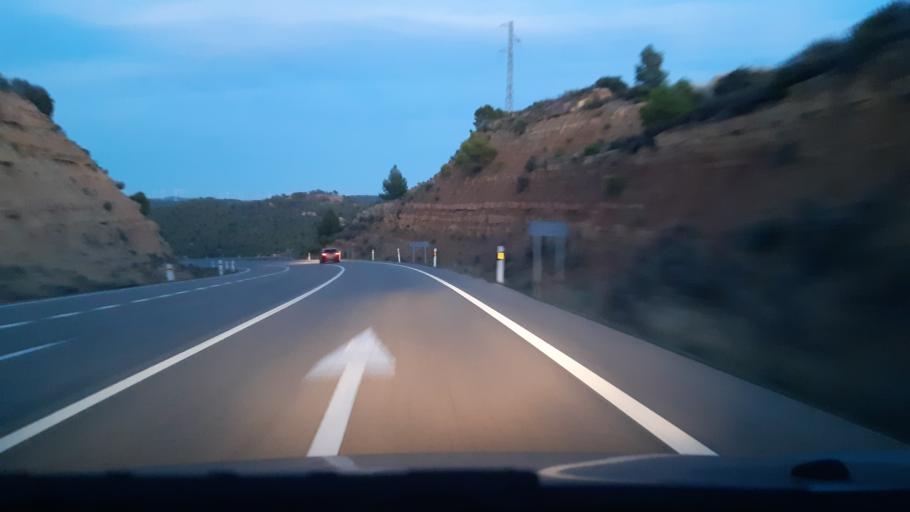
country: ES
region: Aragon
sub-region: Provincia de Teruel
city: Calaceite
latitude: 41.0225
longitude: 0.2189
